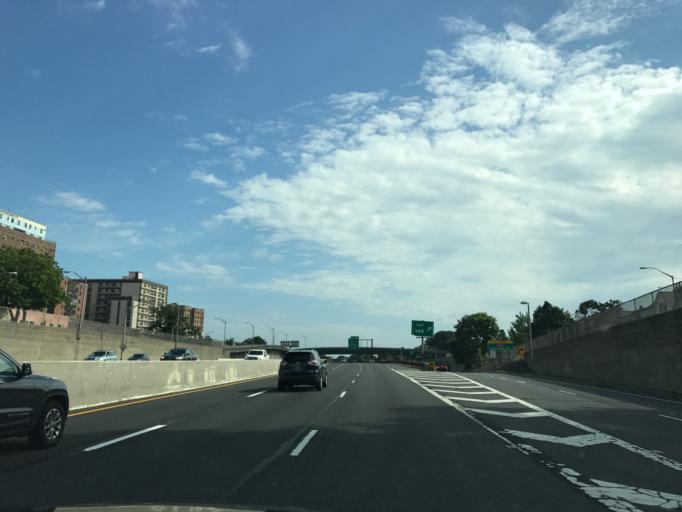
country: US
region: New Jersey
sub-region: Essex County
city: East Orange
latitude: 40.7533
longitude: -74.2108
